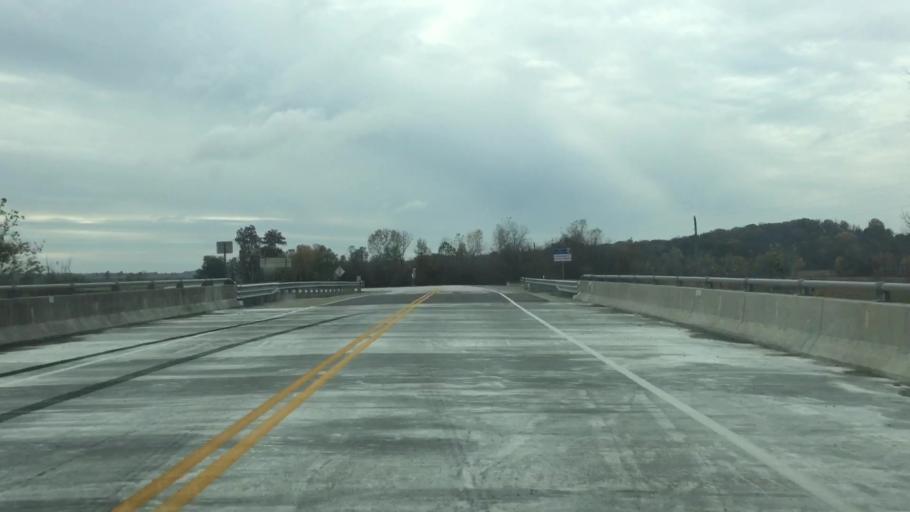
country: US
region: Missouri
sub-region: Gasconade County
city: Hermann
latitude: 38.7289
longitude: -91.4477
